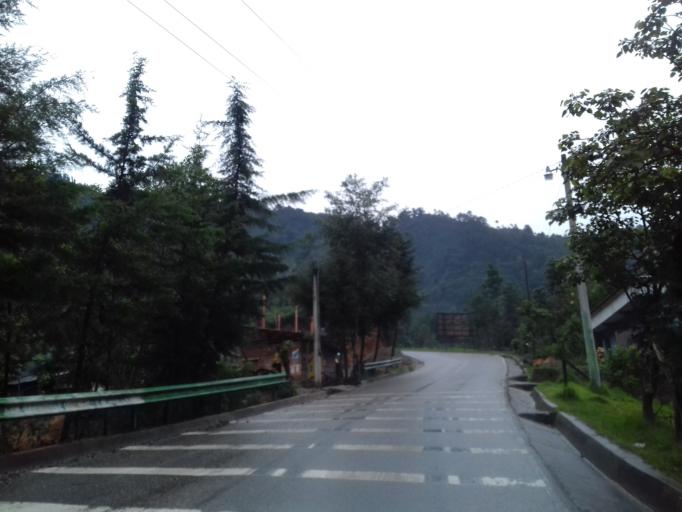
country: GT
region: Quiche
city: Nebaj
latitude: 15.3820
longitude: -91.1104
